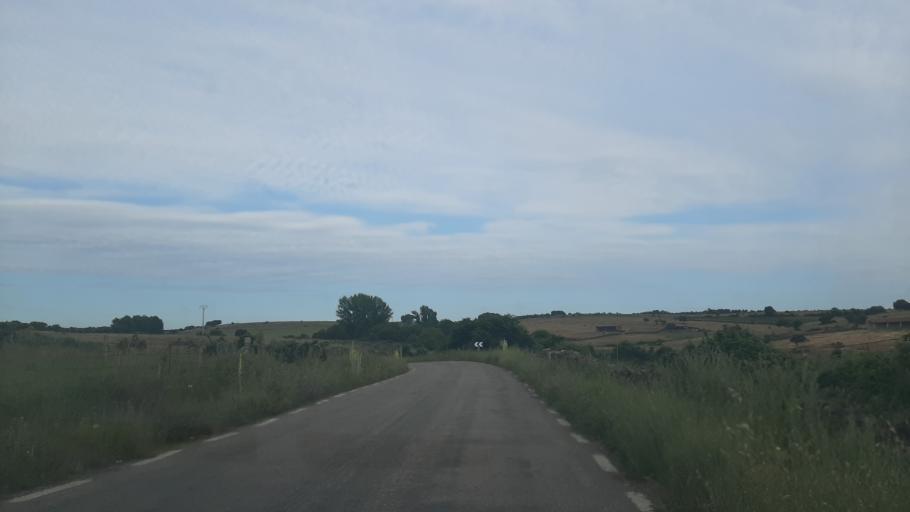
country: ES
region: Castille and Leon
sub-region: Provincia de Salamanca
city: Gallegos de Arganan
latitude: 40.6368
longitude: -6.7204
